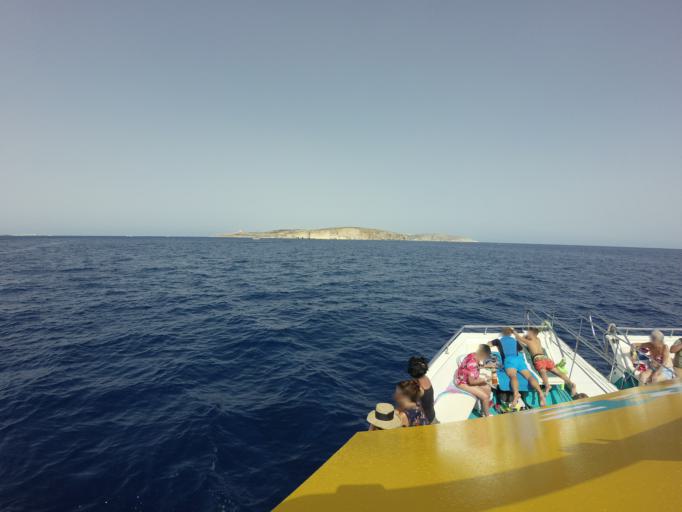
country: MT
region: Il-Mellieha
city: Mellieha
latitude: 36.0023
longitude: 14.3632
